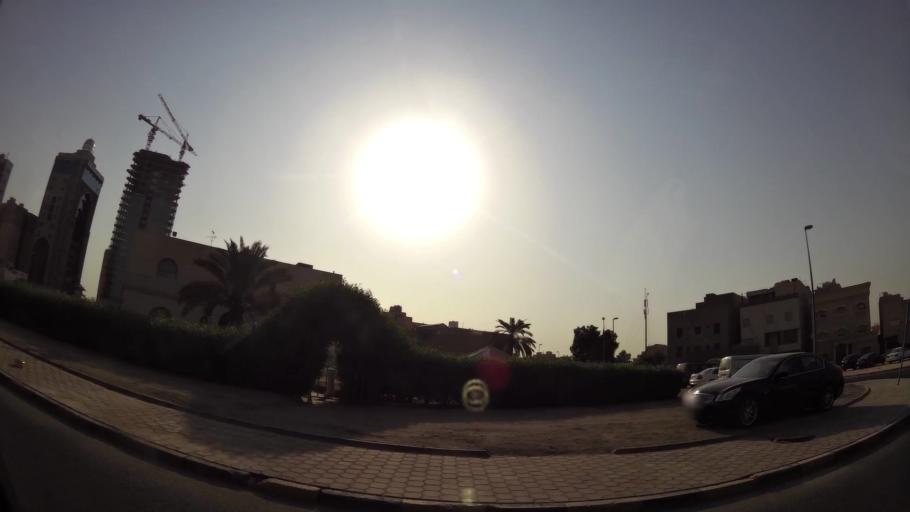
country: KW
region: Al Asimah
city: Ad Dasmah
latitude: 29.3670
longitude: 48.0068
